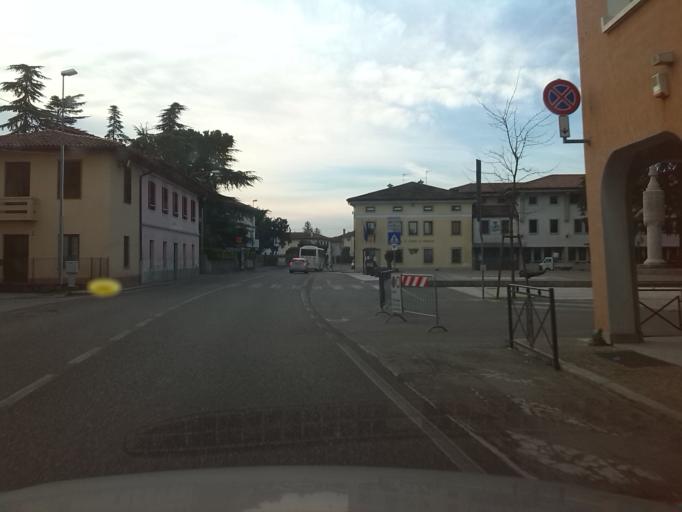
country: IT
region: Friuli Venezia Giulia
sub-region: Provincia di Udine
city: Corno di Rosazzo
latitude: 45.9974
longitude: 13.4414
